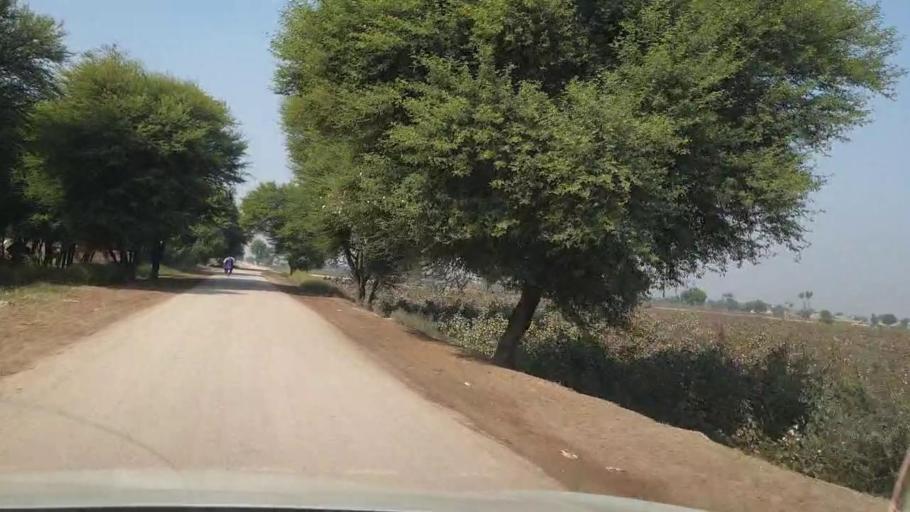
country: PK
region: Sindh
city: Bhan
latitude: 26.5383
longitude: 67.7448
